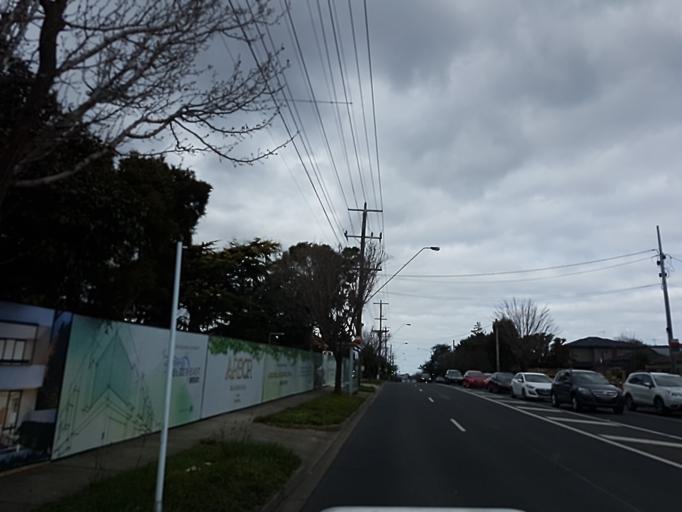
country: AU
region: Victoria
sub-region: Whitehorse
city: Blackburn North
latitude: -37.8126
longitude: 145.1400
